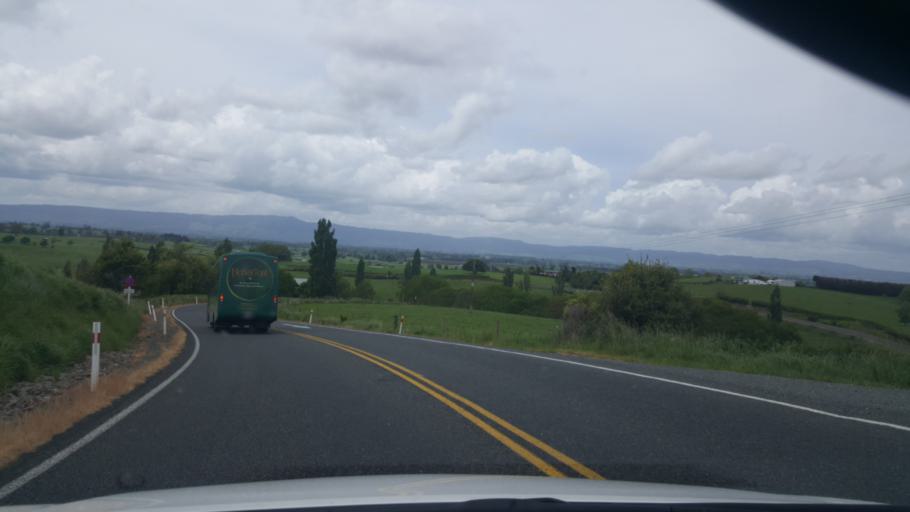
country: NZ
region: Waikato
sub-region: Matamata-Piako District
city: Matamata
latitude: -37.8794
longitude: 175.6906
